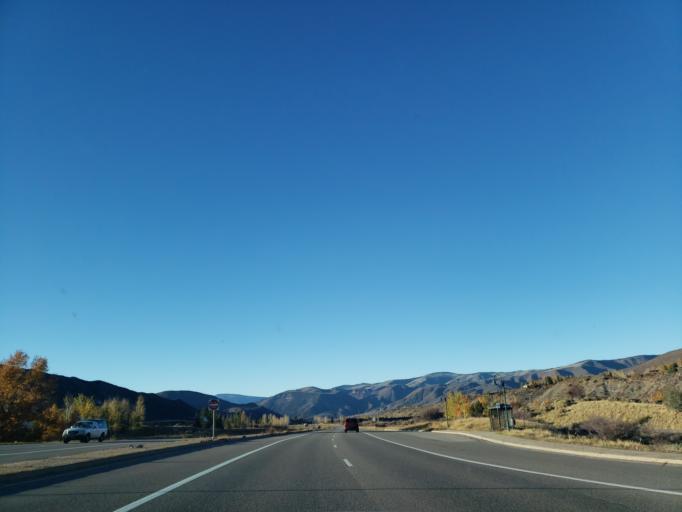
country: US
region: Colorado
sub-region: Pitkin County
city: Aspen
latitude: 39.2245
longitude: -106.8660
